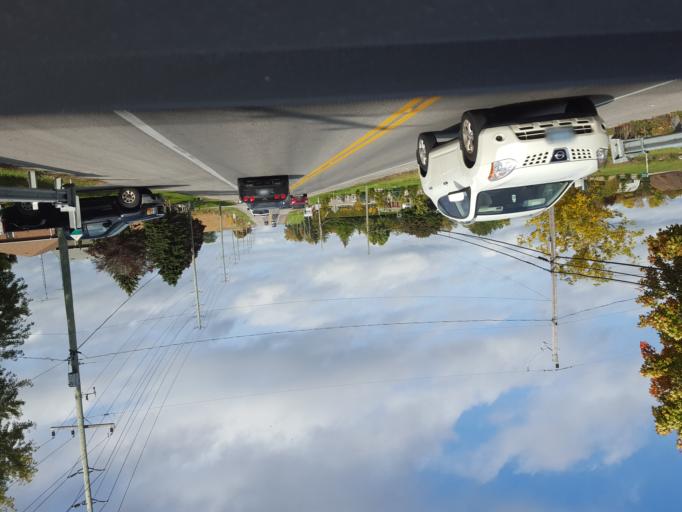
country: CA
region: Ontario
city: Oshawa
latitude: 43.9446
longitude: -78.8269
